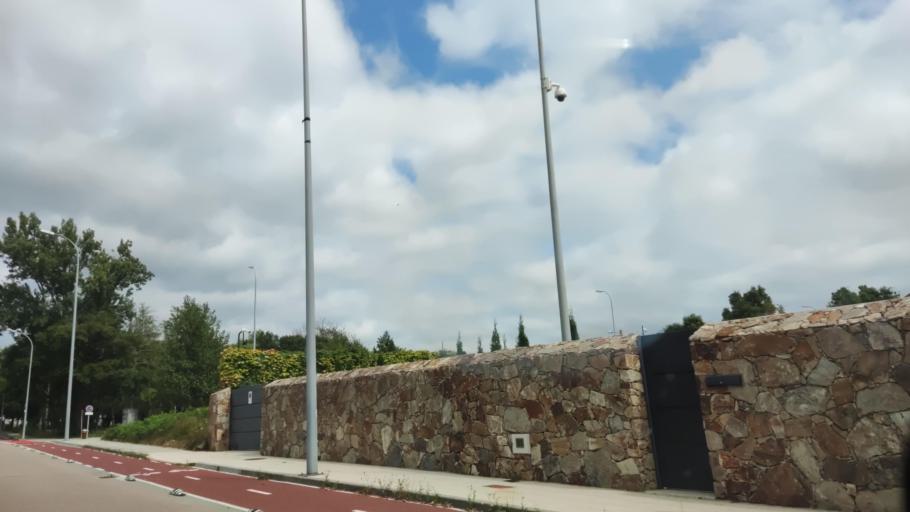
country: ES
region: Galicia
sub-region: Provincia da Coruna
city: Boiro
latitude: 42.6417
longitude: -8.8890
